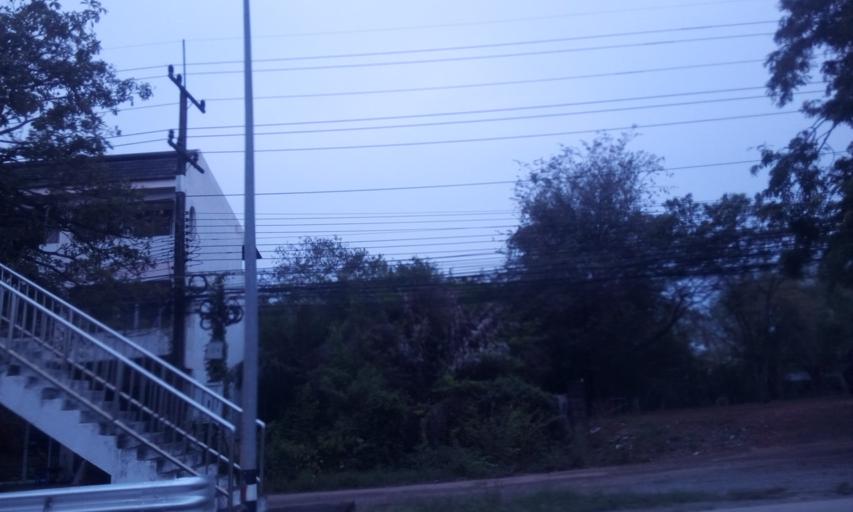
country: TH
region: Chanthaburi
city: Na Yai Am
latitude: 12.7818
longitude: 101.8089
